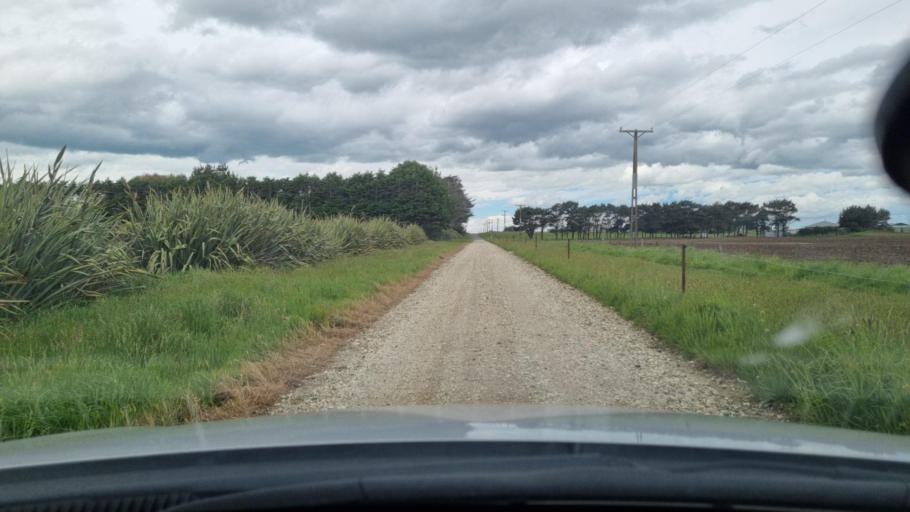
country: NZ
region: Southland
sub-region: Invercargill City
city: Invercargill
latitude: -46.4091
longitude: 168.2562
